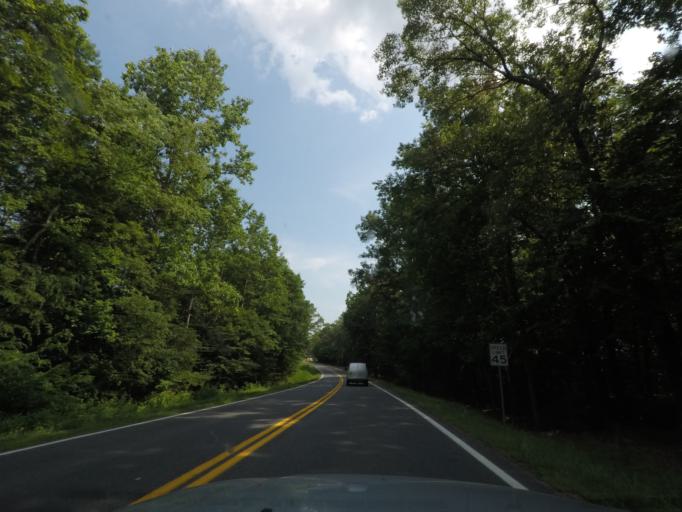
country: US
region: Virginia
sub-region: Fluvanna County
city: Palmyra
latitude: 37.8786
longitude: -78.2629
